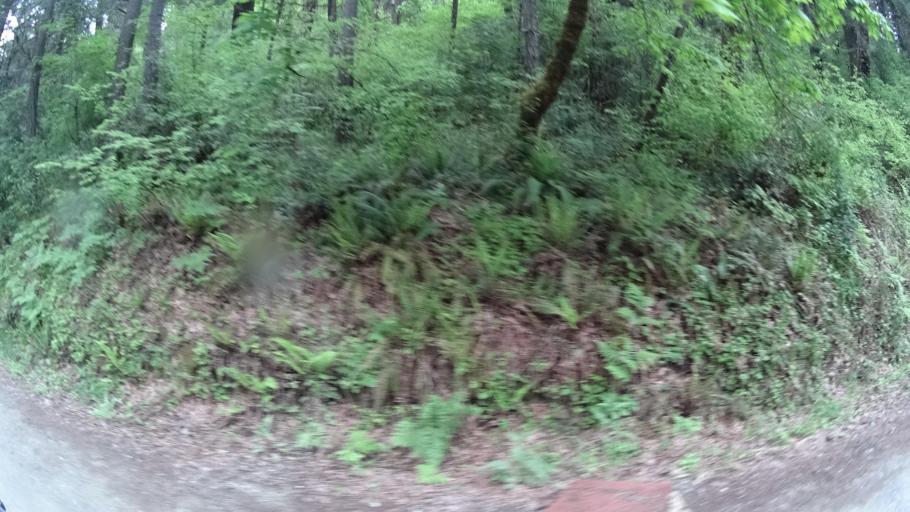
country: US
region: California
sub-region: Humboldt County
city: Willow Creek
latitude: 41.1255
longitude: -123.7481
